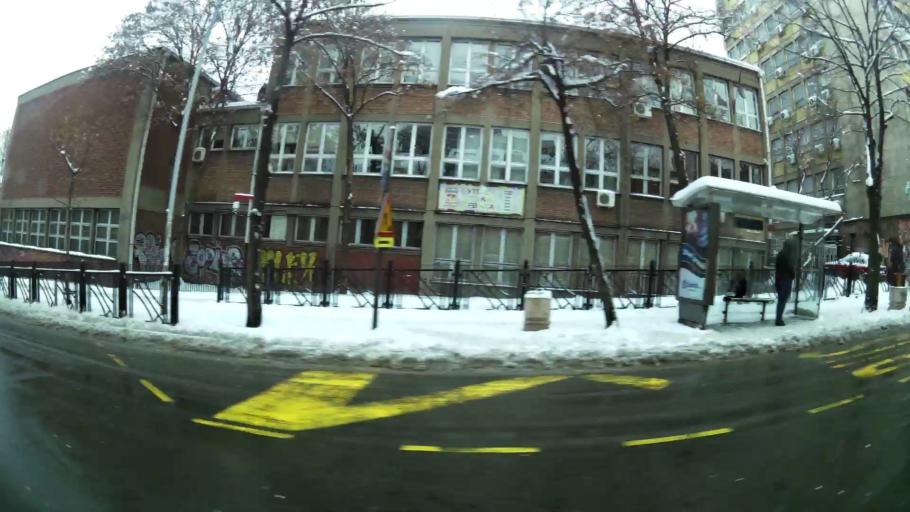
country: RS
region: Central Serbia
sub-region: Belgrade
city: Stari Grad
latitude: 44.8190
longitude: 20.4647
